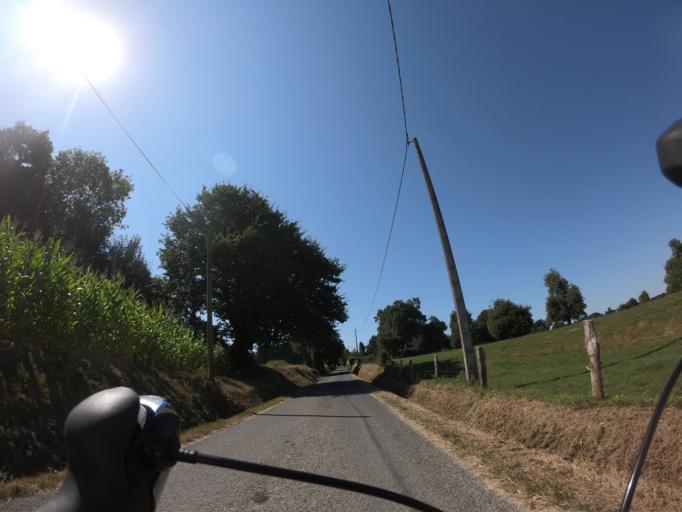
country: FR
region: Lower Normandy
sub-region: Departement de la Manche
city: Barenton
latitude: 48.5685
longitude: -0.7992
